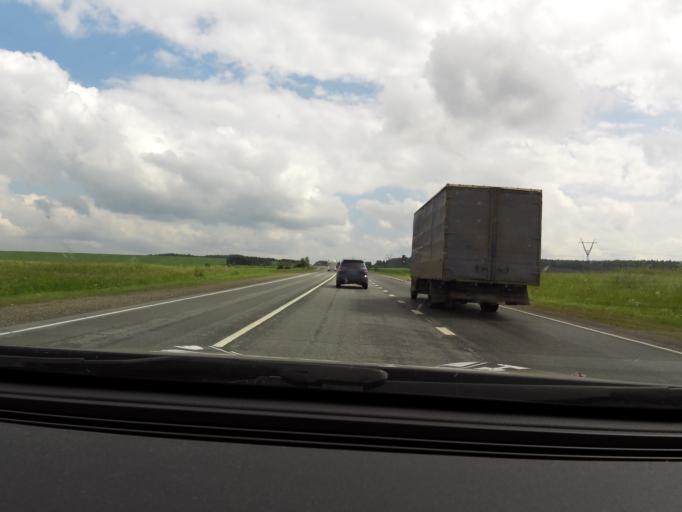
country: RU
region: Sverdlovsk
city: Achit
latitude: 56.8839
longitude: 57.6206
